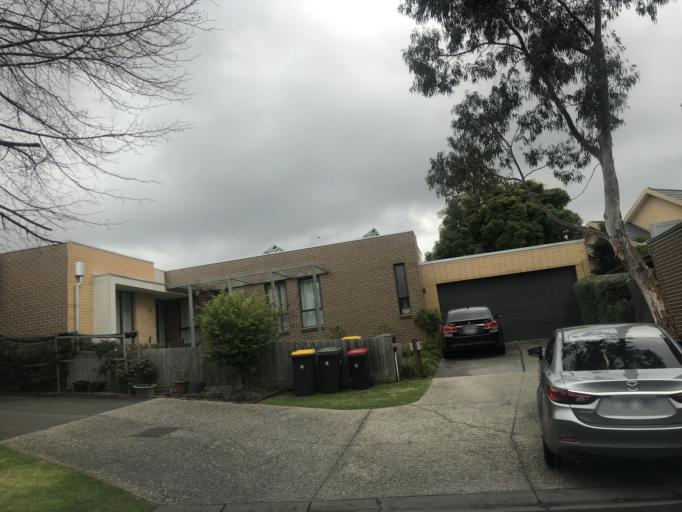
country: AU
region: Victoria
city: Burwood East
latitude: -37.8595
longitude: 145.1446
